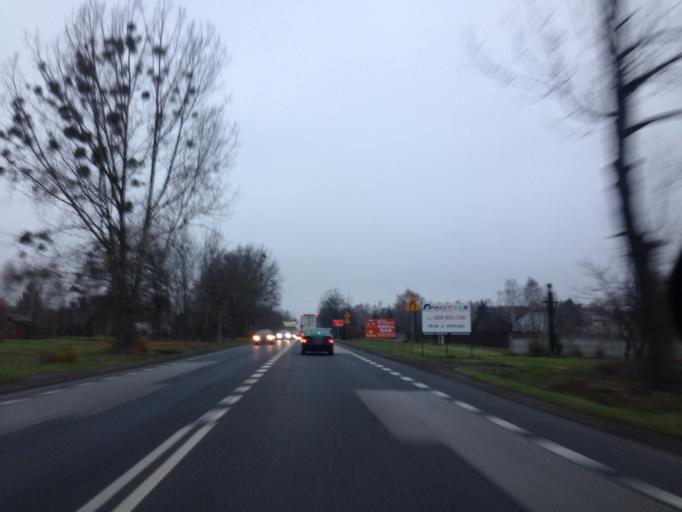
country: PL
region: Lodz Voivodeship
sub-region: Powiat zgierski
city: Strykow
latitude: 51.8307
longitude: 19.5329
